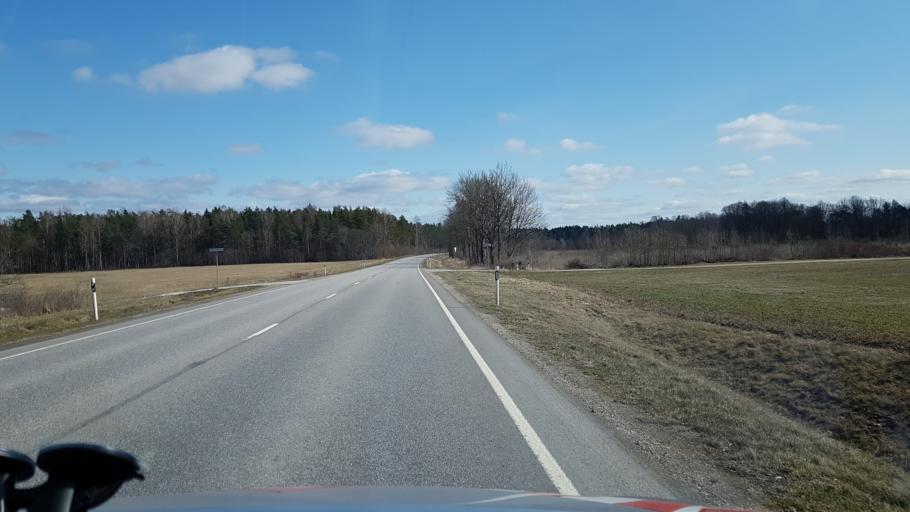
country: EE
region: Laeaene
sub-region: Ridala Parish
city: Uuemoisa
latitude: 58.9599
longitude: 23.7078
